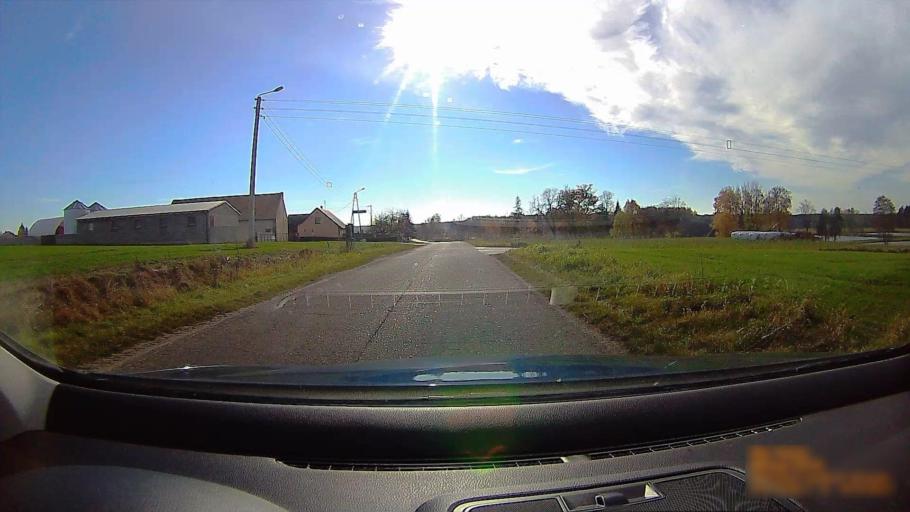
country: PL
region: Greater Poland Voivodeship
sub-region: Powiat ostrzeszowski
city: Doruchow
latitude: 51.3967
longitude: 18.0304
